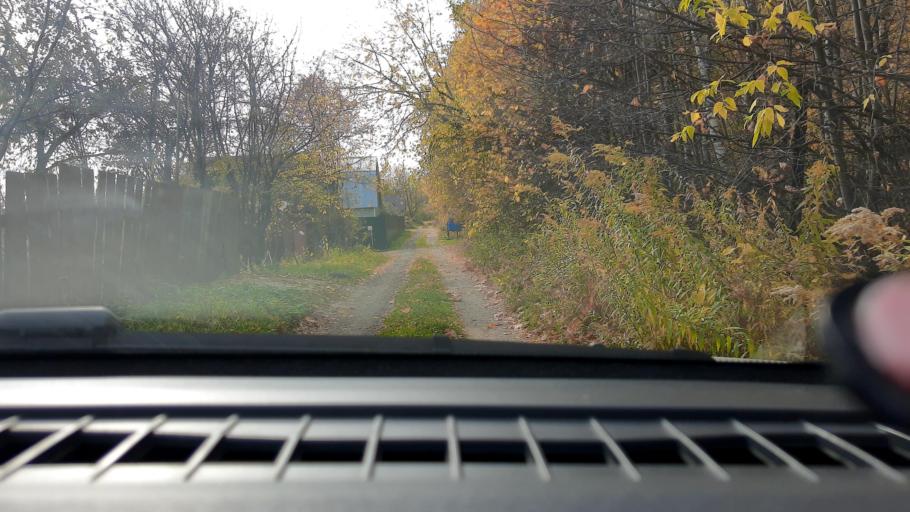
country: RU
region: Nizjnij Novgorod
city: Afonino
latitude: 56.2195
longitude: 44.0807
